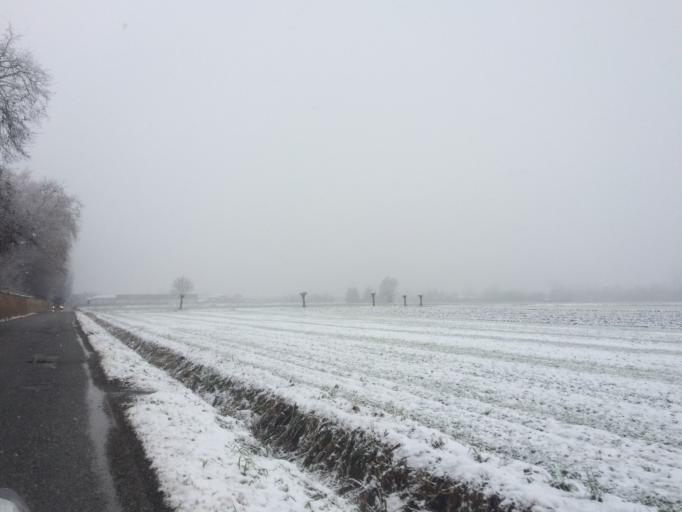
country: IT
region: Piedmont
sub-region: Provincia di Cuneo
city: Racconigi
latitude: 44.7747
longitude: 7.6702
